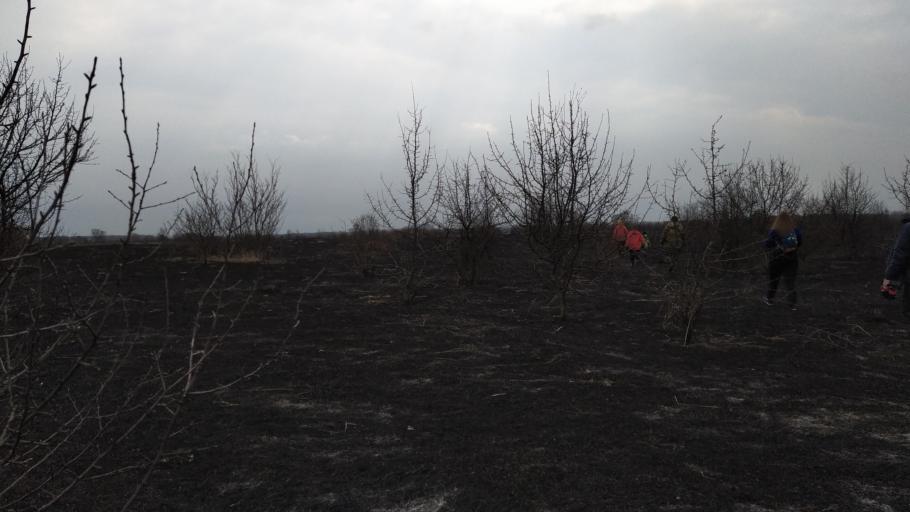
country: RU
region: Rostov
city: Semikarakorsk
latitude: 47.5524
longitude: 40.6754
